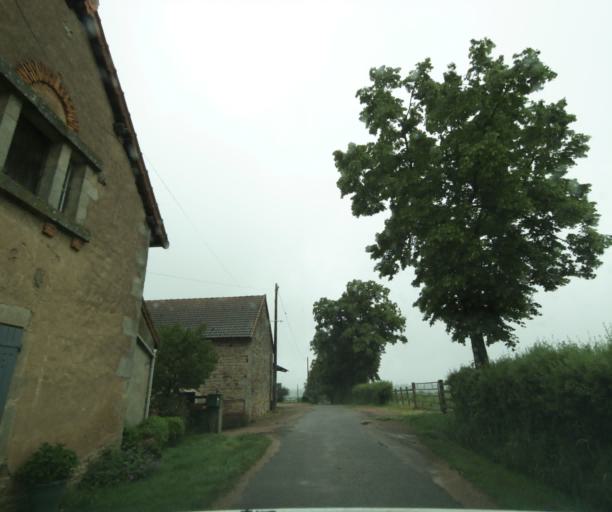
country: FR
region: Bourgogne
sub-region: Departement de Saone-et-Loire
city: Charolles
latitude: 46.4334
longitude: 4.3674
